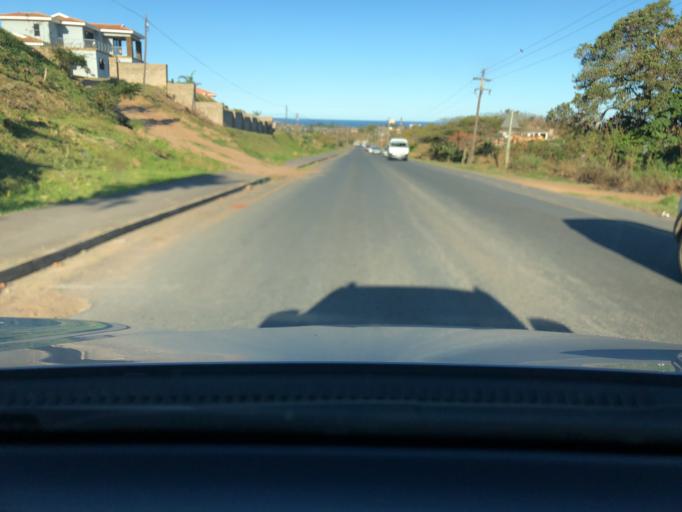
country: ZA
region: KwaZulu-Natal
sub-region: eThekwini Metropolitan Municipality
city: Umkomaas
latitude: -30.0350
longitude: 30.8468
